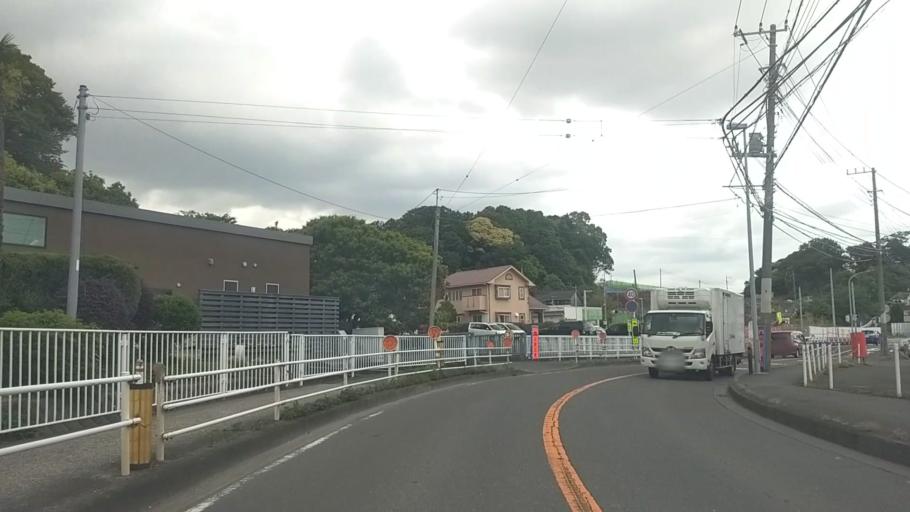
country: JP
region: Kanagawa
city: Fujisawa
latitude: 35.3692
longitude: 139.5220
